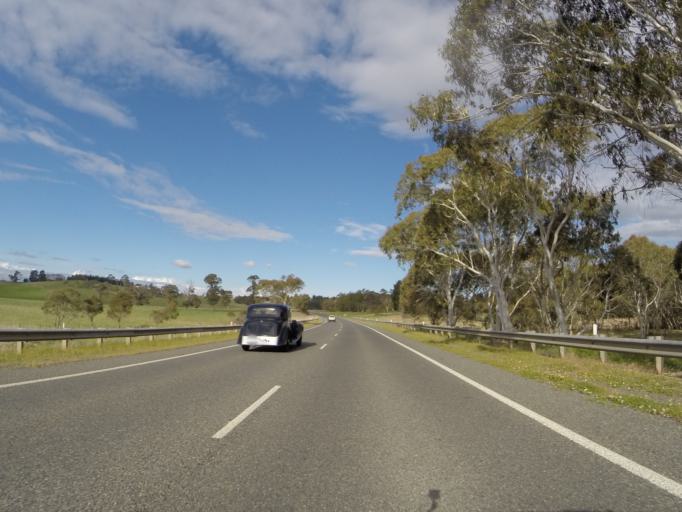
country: AU
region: New South Wales
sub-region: Wingecarribee
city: Bundanoon
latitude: -34.5863
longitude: 150.2630
